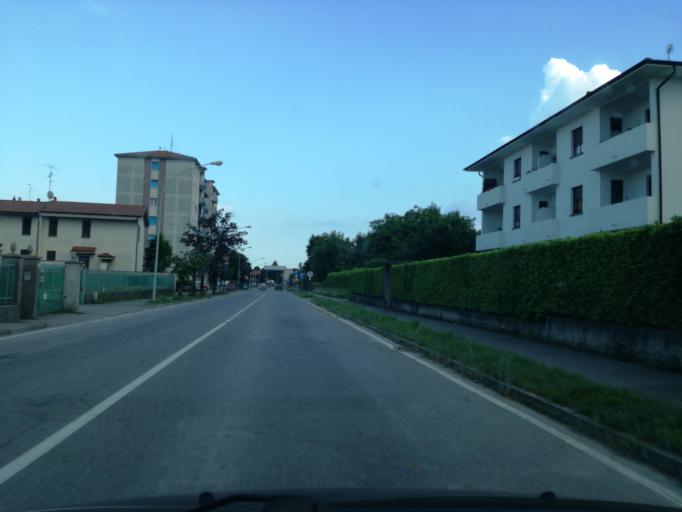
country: IT
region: Lombardy
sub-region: Provincia di Monza e Brianza
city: Porto d'Adda
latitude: 45.6495
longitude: 9.4625
